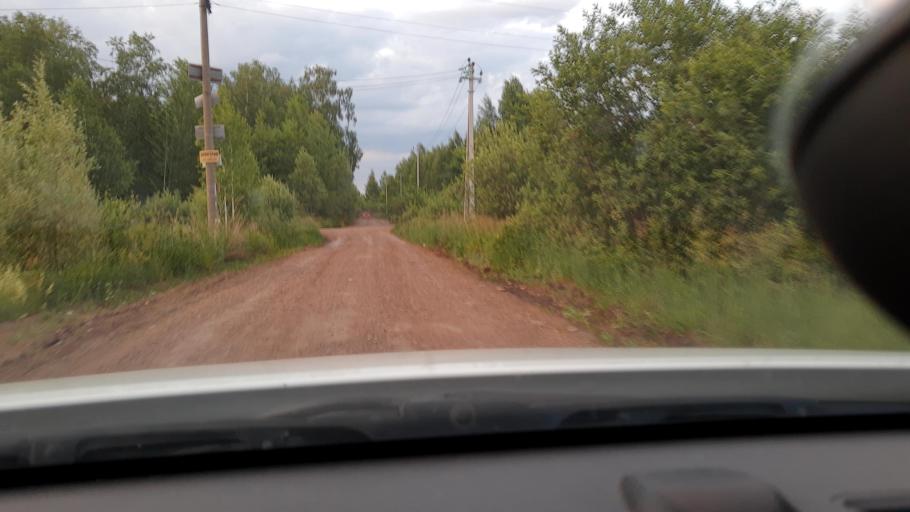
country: RU
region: Bashkortostan
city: Kabakovo
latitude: 54.4420
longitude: 55.9117
